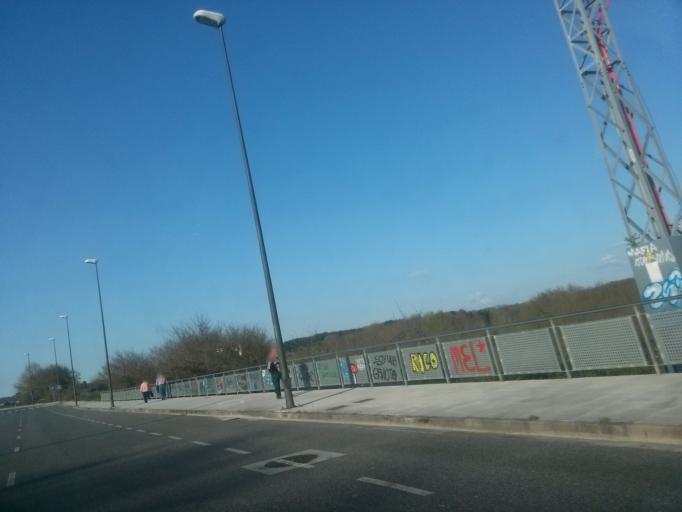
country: ES
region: Galicia
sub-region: Provincia de Lugo
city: Lugo
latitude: 42.9978
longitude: -7.5388
